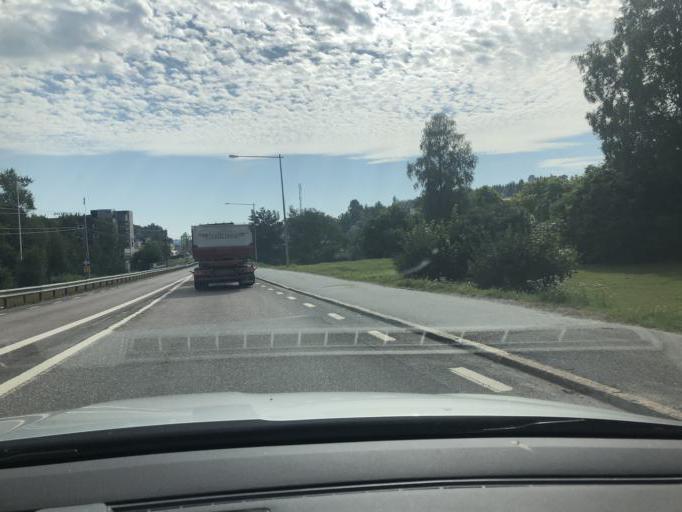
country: SE
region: Vaesternorrland
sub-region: Kramfors Kommun
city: Kramfors
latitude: 62.9337
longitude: 17.7722
